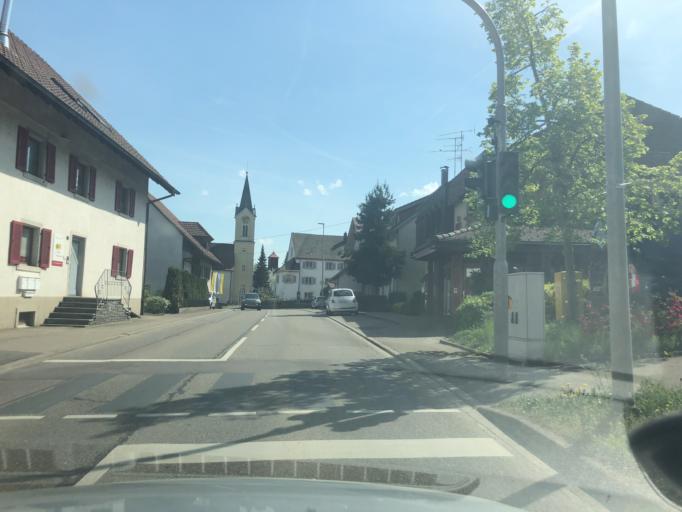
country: DE
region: Baden-Wuerttemberg
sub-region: Freiburg Region
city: Weilheim
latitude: 47.6427
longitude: 8.2463
